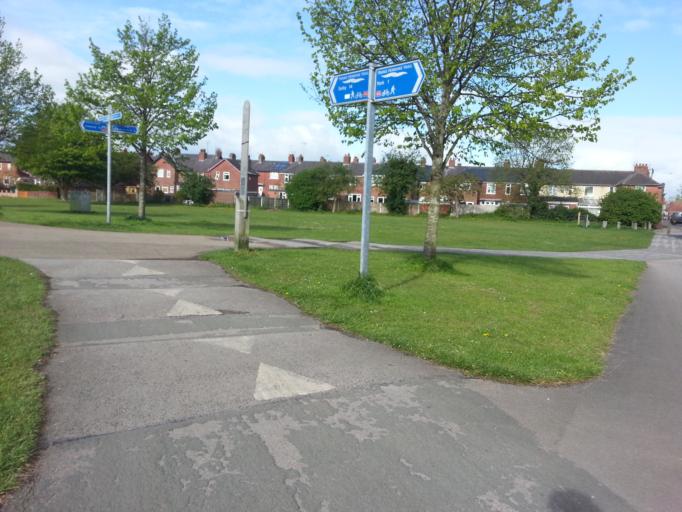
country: GB
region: England
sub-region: City of York
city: York
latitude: 53.9456
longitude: -1.0830
